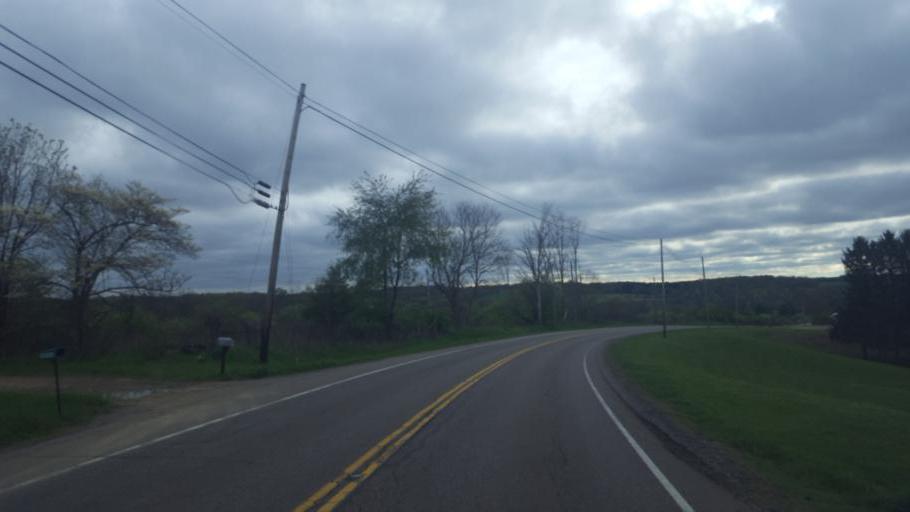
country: US
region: Ohio
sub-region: Knox County
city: Gambier
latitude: 40.4136
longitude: -82.3904
